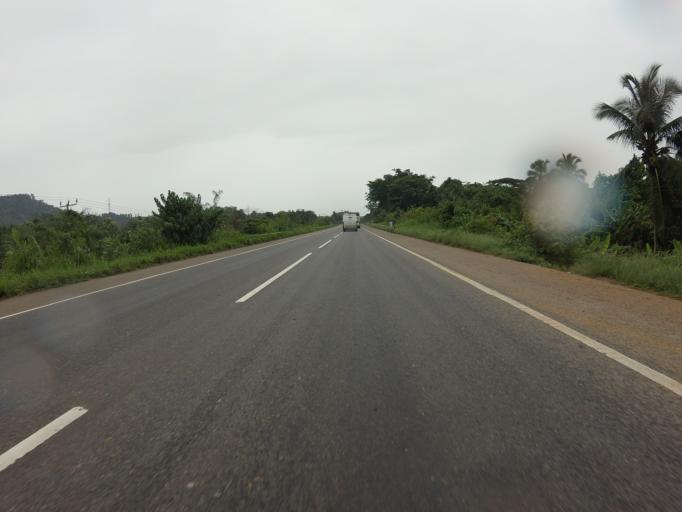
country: GH
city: Kibi
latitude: 6.1326
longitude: -0.4947
